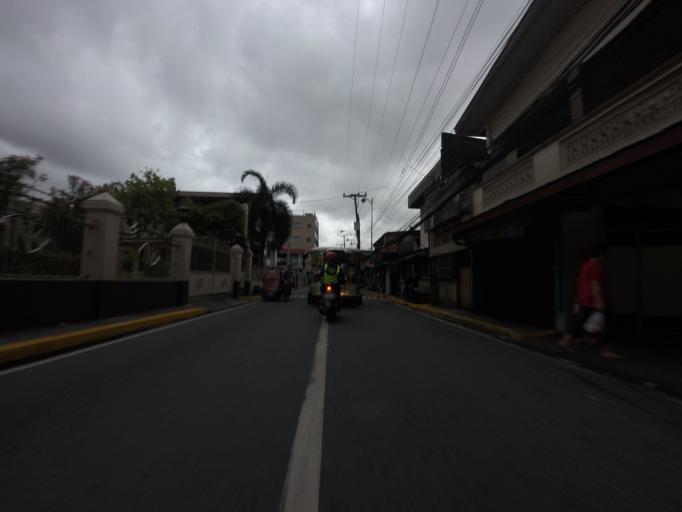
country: PH
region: Metro Manila
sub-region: San Juan
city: San Juan
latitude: 14.5875
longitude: 121.0166
